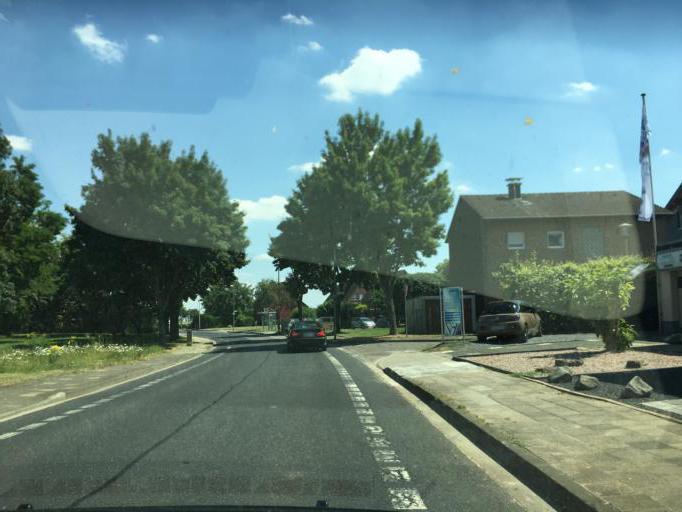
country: DE
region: North Rhine-Westphalia
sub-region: Regierungsbezirk Koln
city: Dueren
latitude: 50.7926
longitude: 6.4241
